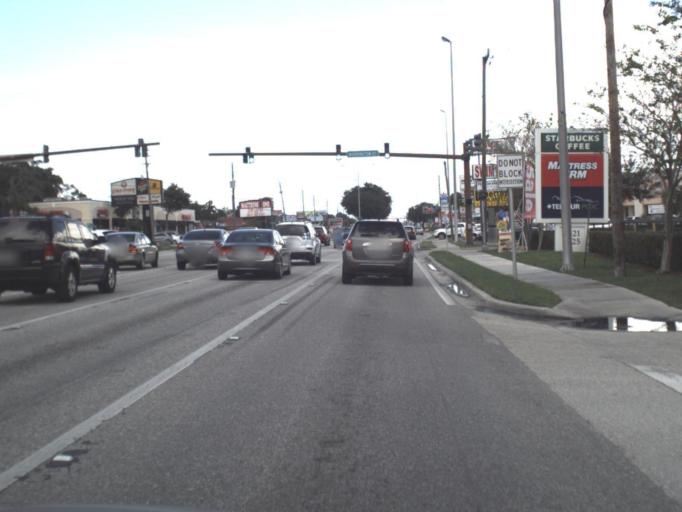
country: US
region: Florida
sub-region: Sarasota County
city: South Sarasota
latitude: 27.2911
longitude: -82.5306
